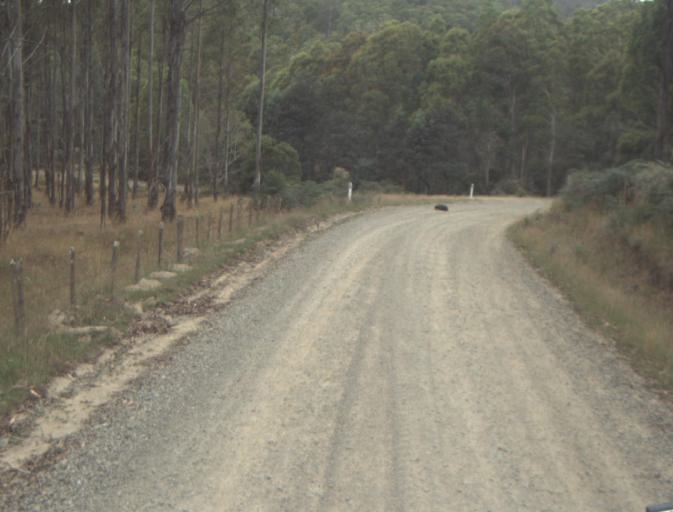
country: AU
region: Tasmania
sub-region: Dorset
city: Scottsdale
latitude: -41.4164
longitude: 147.5224
